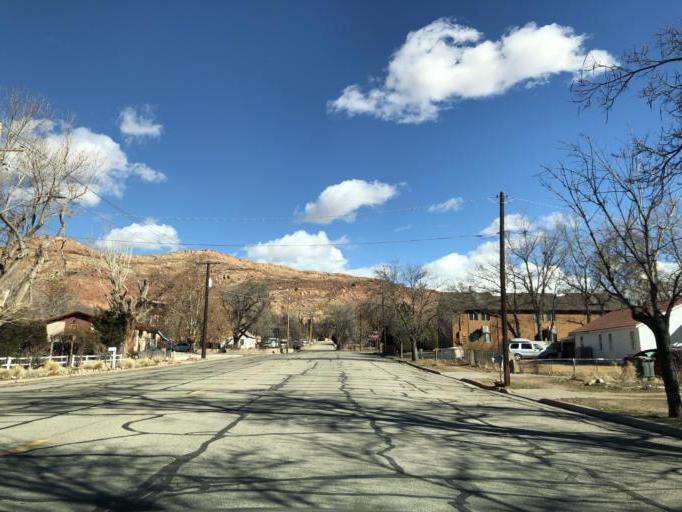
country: US
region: Utah
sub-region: Grand County
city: Moab
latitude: 38.5733
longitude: -109.5443
